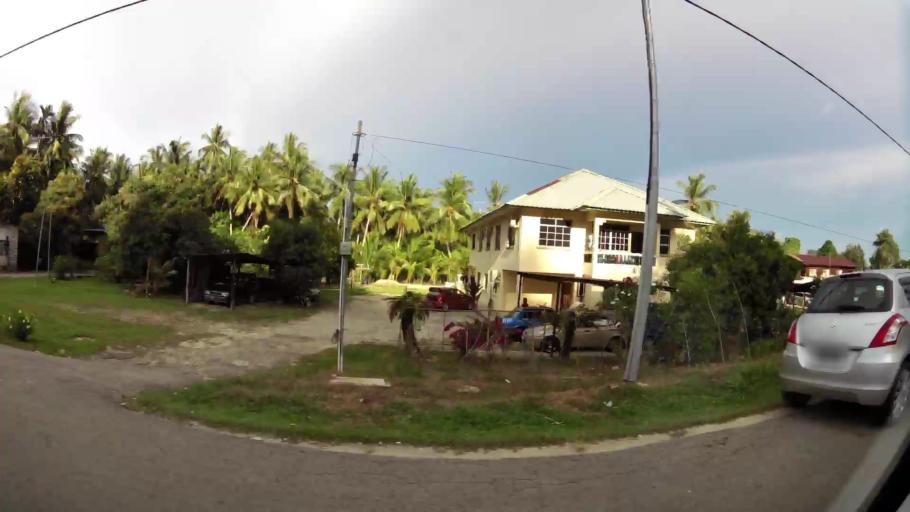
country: BN
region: Brunei and Muara
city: Bandar Seri Begawan
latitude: 4.9679
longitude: 115.0206
